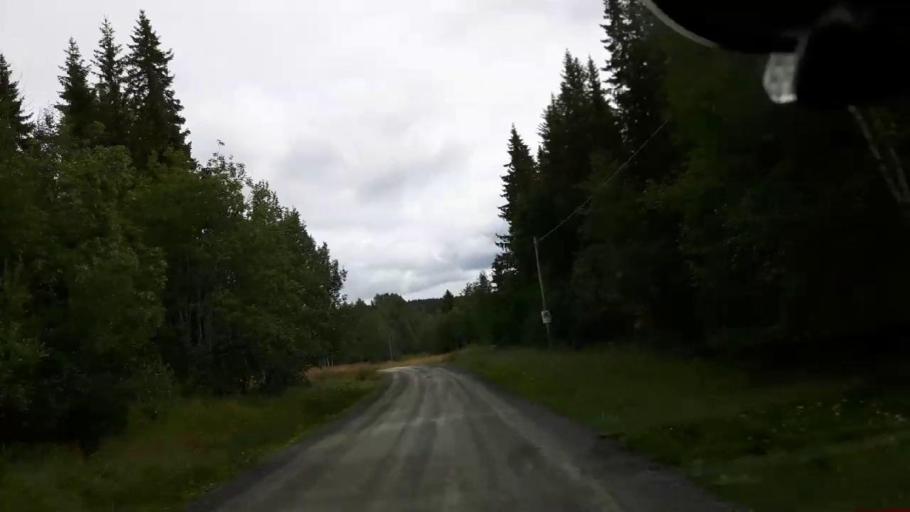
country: SE
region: Jaemtland
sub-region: Krokoms Kommun
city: Valla
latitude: 63.6741
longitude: 13.9425
